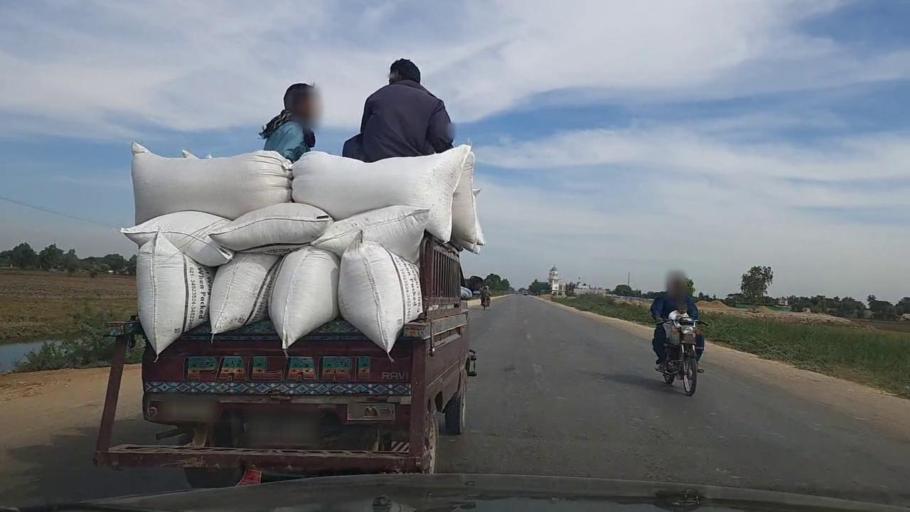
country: PK
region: Sindh
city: Thatta
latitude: 24.7822
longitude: 67.9494
